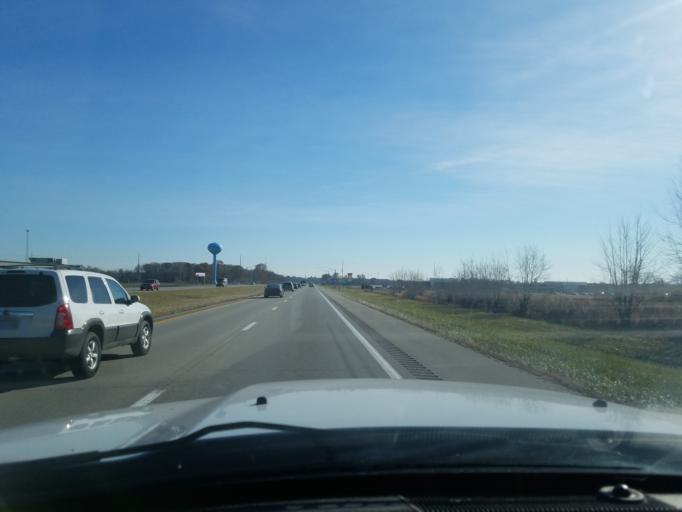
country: US
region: Ohio
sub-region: Brown County
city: Mount Orab
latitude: 39.0471
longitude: -83.9443
